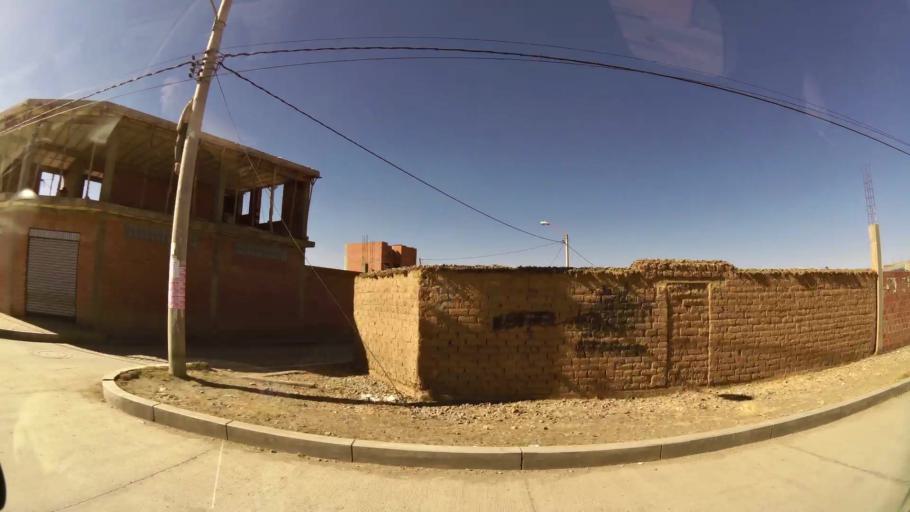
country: BO
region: La Paz
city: La Paz
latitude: -16.5335
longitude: -68.2260
